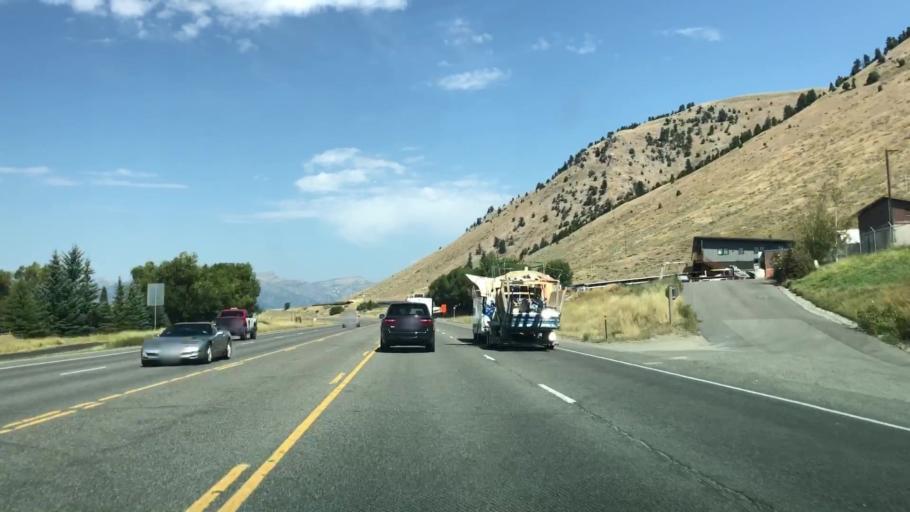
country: US
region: Wyoming
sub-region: Teton County
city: South Park
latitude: 43.4273
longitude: -110.7788
